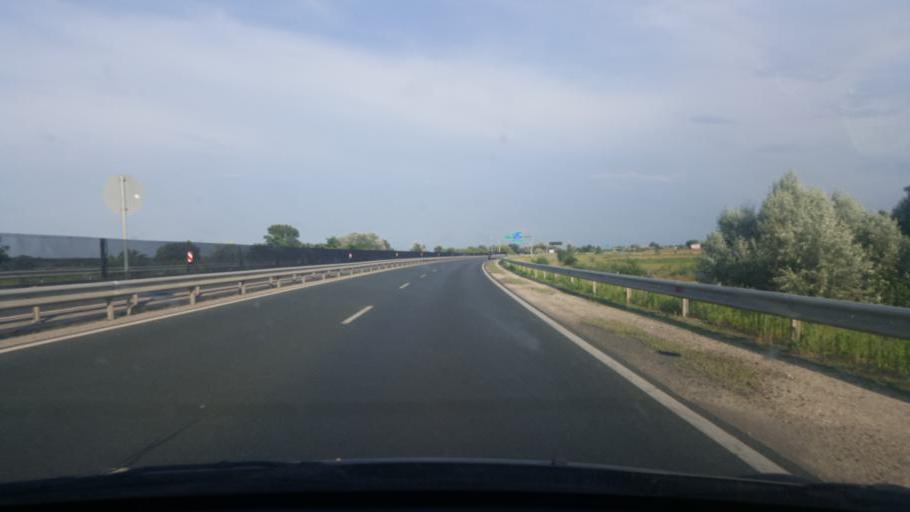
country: HU
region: Pest
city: Vecses
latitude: 47.4128
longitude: 19.2911
